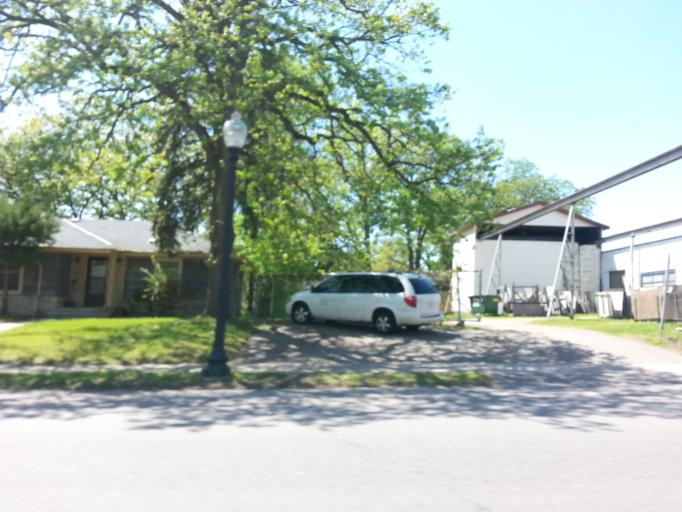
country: US
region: Minnesota
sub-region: Hennepin County
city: Richfield
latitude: 44.9229
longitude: -93.2626
